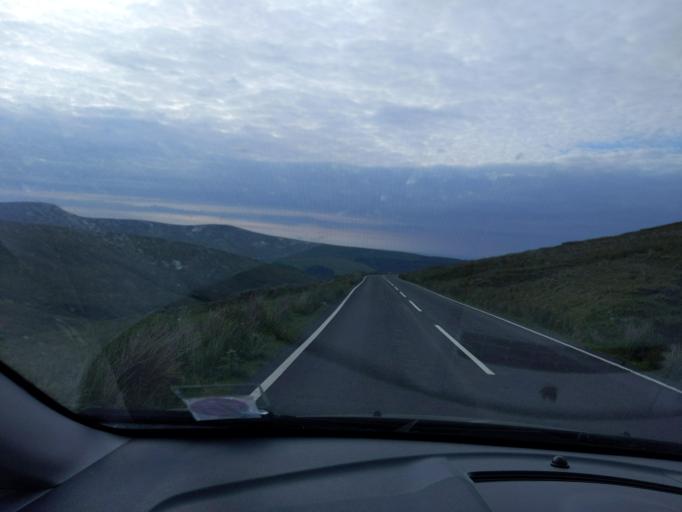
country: IM
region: Laxey
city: Laxey
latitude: 54.2547
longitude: -4.4722
